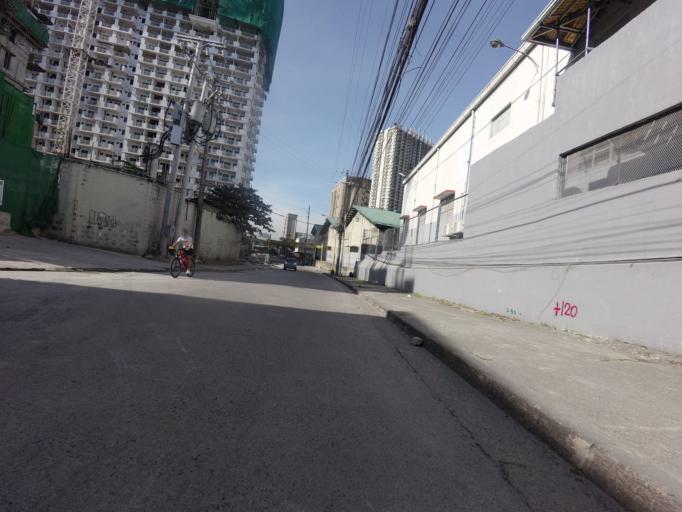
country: PH
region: Metro Manila
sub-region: Pasig
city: Pasig City
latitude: 14.5703
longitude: 121.0547
